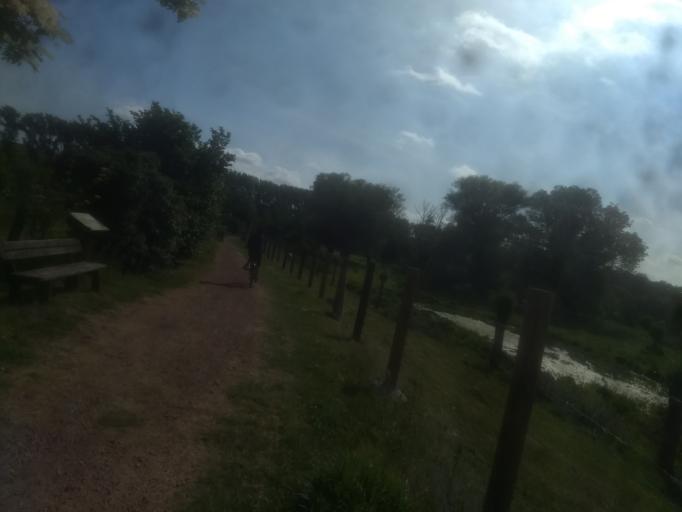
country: FR
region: Nord-Pas-de-Calais
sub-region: Departement du Pas-de-Calais
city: Saint-Laurent-Blangy
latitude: 50.3034
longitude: 2.8224
